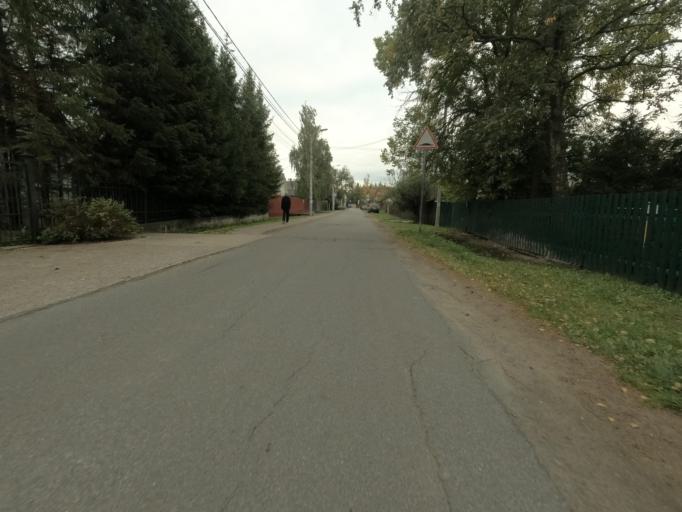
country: RU
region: St.-Petersburg
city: Ust'-Izhora
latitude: 59.8096
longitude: 30.5900
